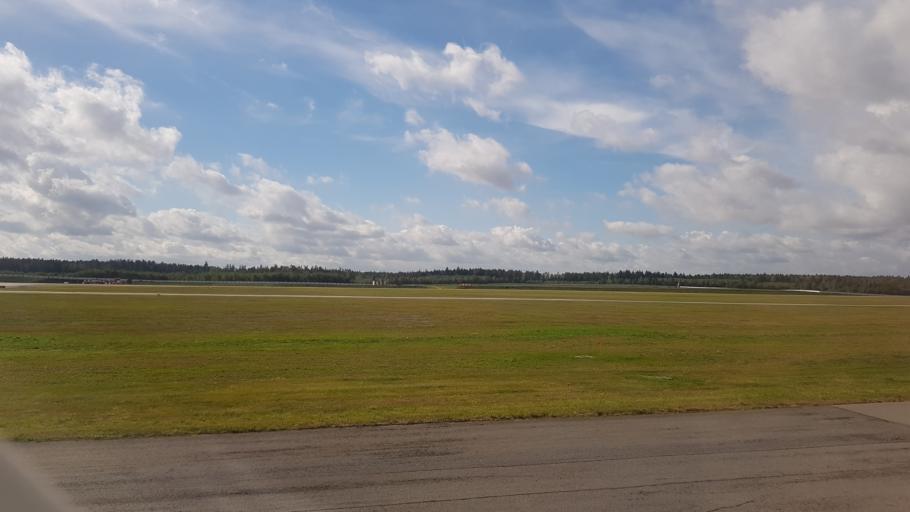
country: BY
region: Minsk
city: Smilavichy
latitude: 53.8858
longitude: 28.0338
